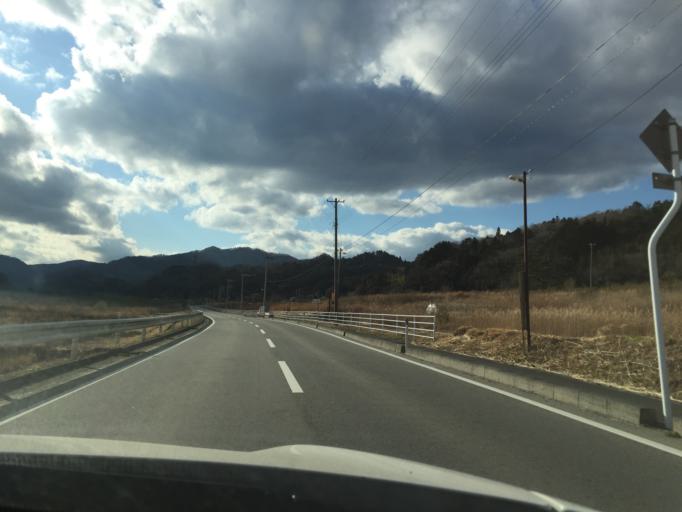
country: JP
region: Fukushima
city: Namie
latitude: 37.4130
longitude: 140.9574
